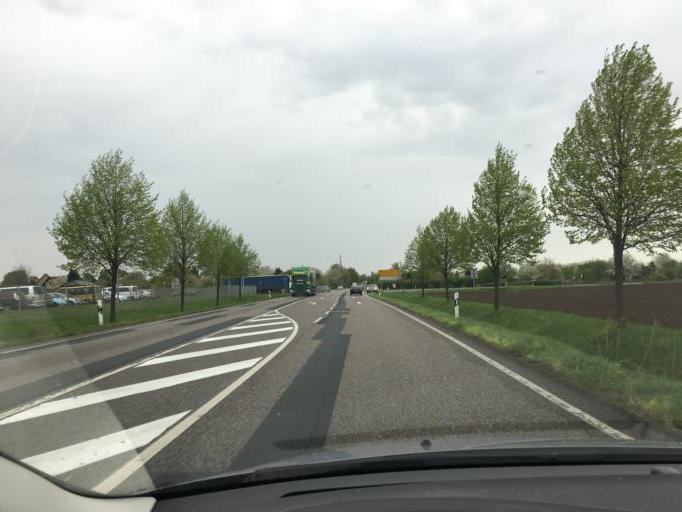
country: DE
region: Saxony-Anhalt
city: Gross Ammensleben
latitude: 52.2296
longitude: 11.5298
